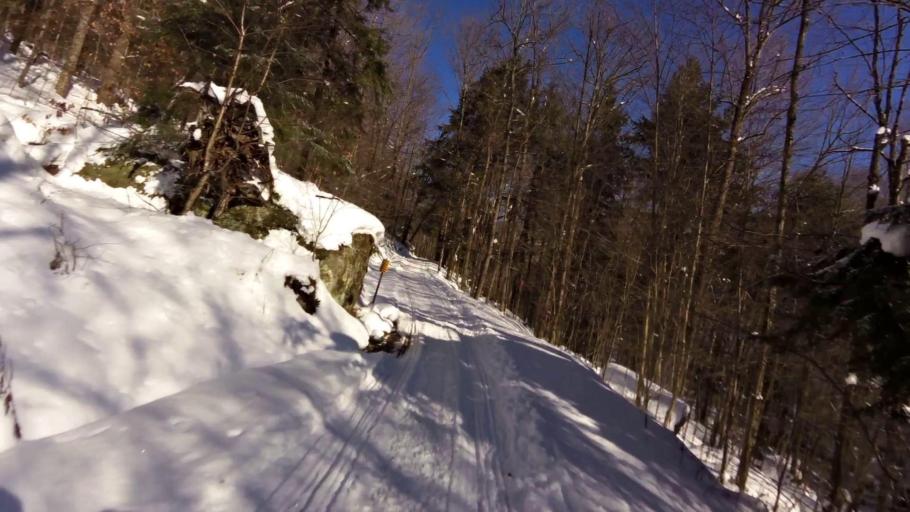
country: US
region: Pennsylvania
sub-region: McKean County
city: Bradford
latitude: 42.0133
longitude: -78.7947
